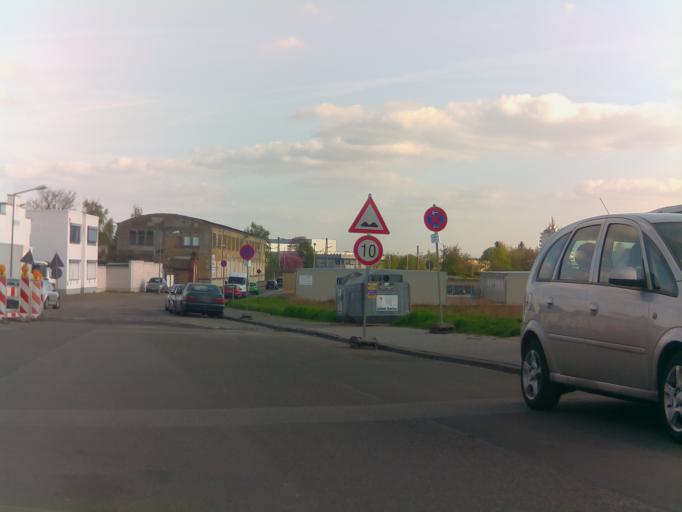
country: DE
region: Rheinland-Pfalz
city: Worms
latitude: 49.6254
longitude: 8.3526
